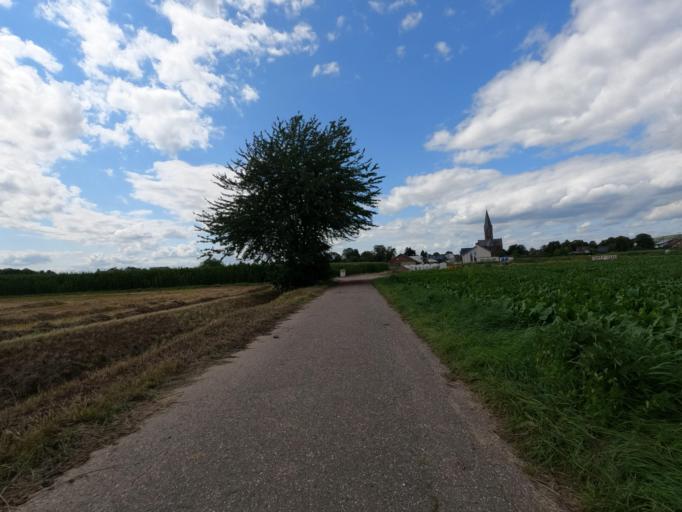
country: DE
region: North Rhine-Westphalia
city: Huckelhoven
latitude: 51.0344
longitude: 6.2243
